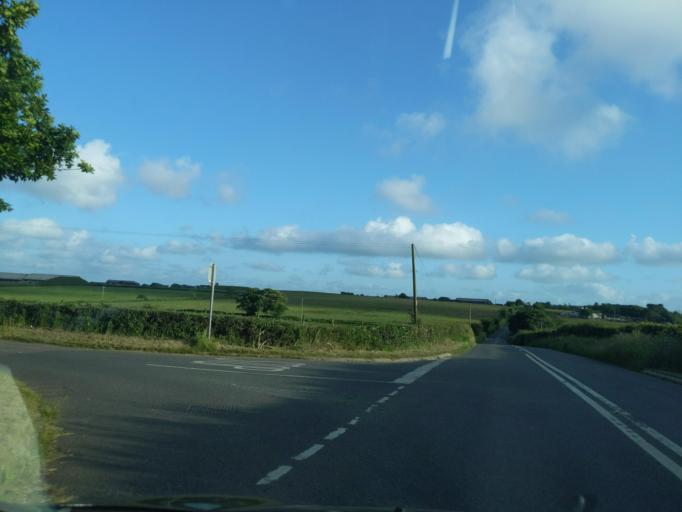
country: GB
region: England
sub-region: Devon
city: Great Torrington
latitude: 50.9849
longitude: -4.0928
